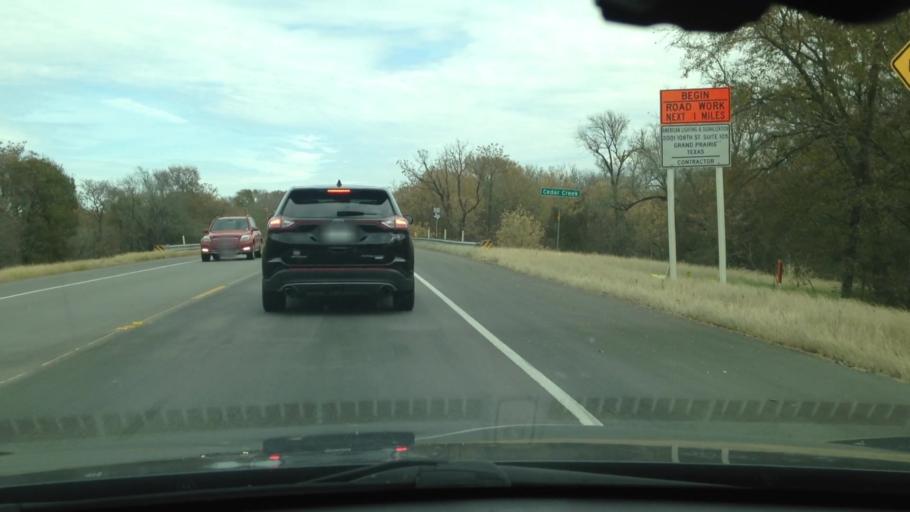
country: US
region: Texas
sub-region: Bastrop County
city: Wyldwood
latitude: 30.0860
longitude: -97.5069
